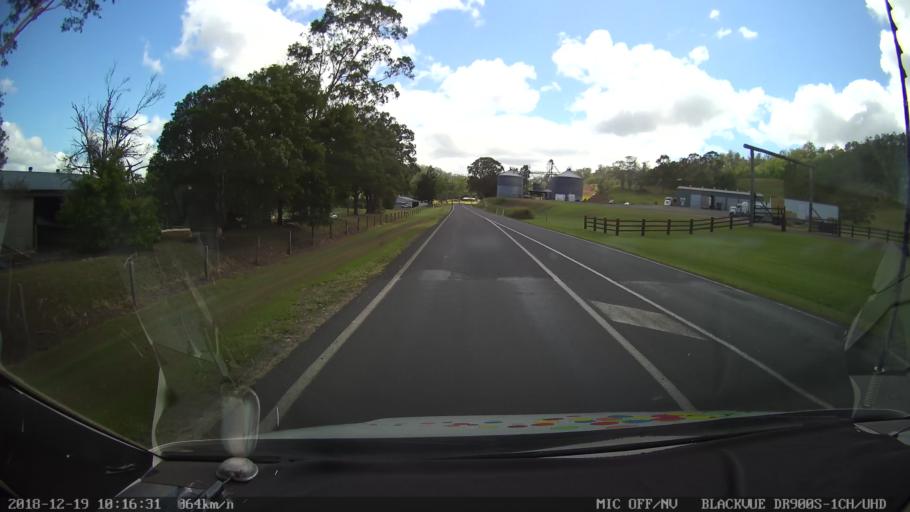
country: AU
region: New South Wales
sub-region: Kyogle
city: Kyogle
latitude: -28.6074
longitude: 153.0222
